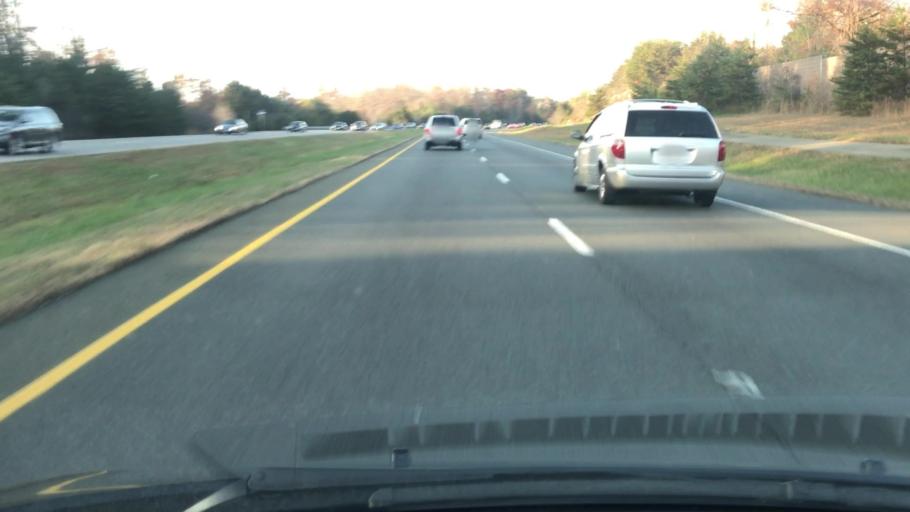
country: US
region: Virginia
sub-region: Prince William County
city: Lake Ridge
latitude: 38.7231
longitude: -77.2803
